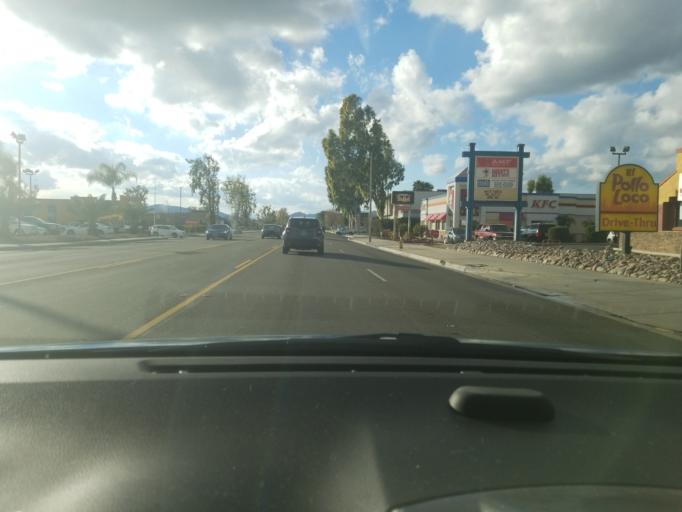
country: US
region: California
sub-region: Riverside County
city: Hemet
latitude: 33.7474
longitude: -117.0013
